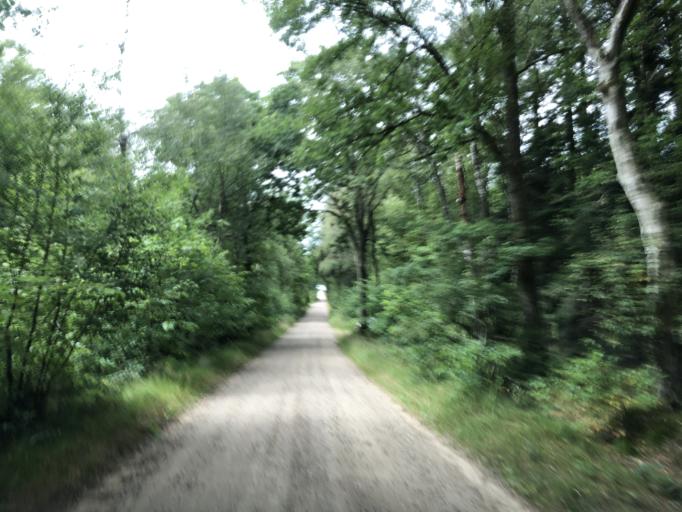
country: DK
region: Central Jutland
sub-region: Holstebro Kommune
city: Holstebro
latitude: 56.2455
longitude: 8.5033
